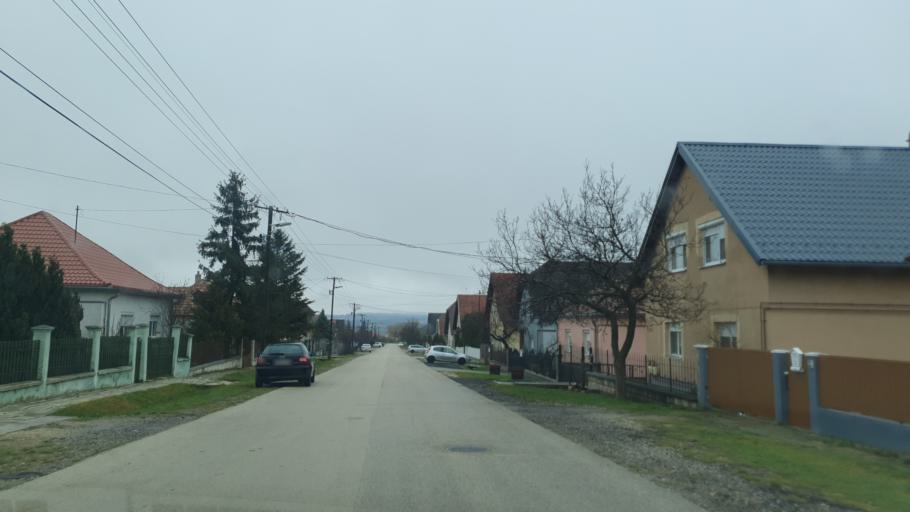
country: HU
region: Veszprem
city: Hajmasker
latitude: 47.1461
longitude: 17.9549
